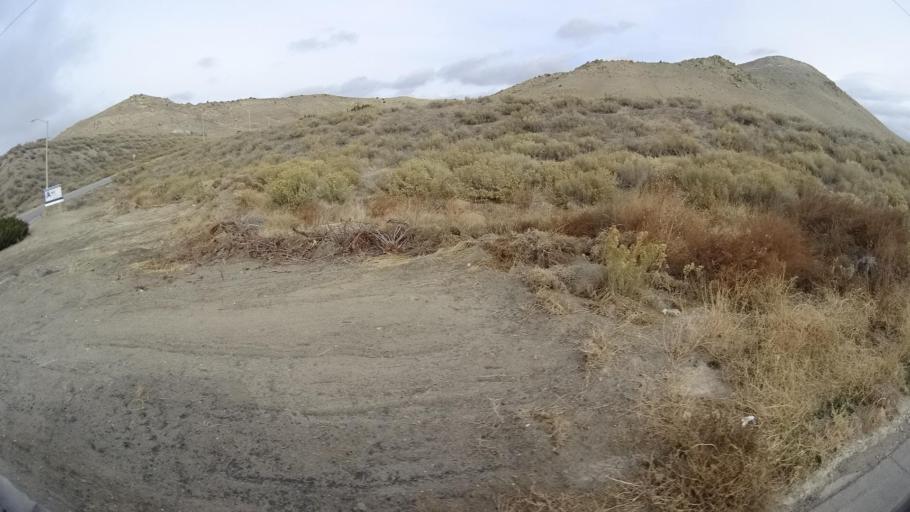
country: US
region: California
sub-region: Kern County
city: Tehachapi
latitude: 35.1209
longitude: -118.3599
